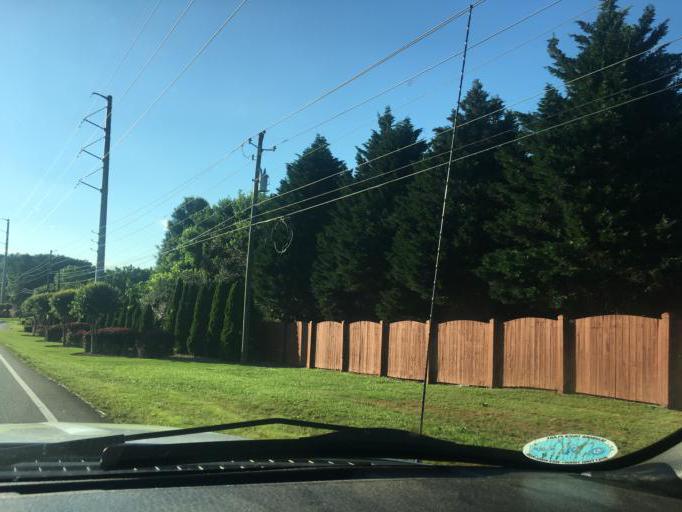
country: US
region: Georgia
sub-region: Forsyth County
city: Cumming
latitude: 34.2803
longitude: -84.1193
